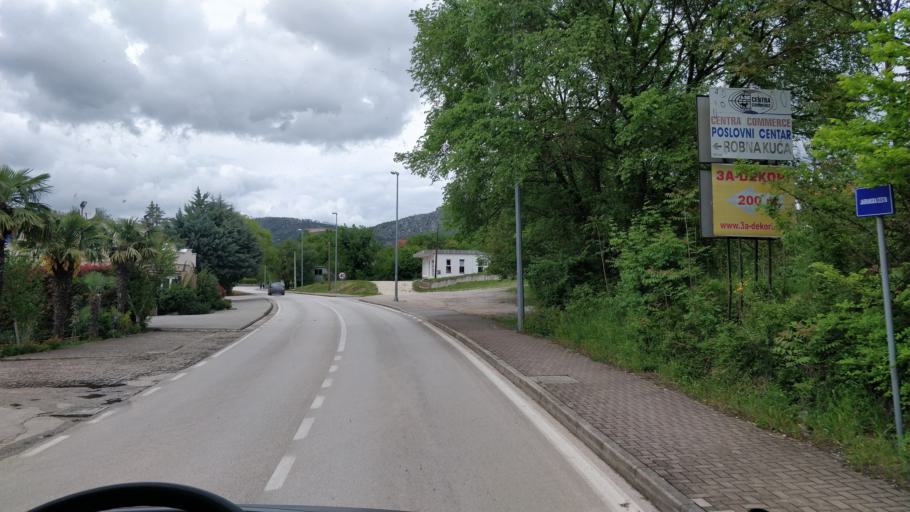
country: BA
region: Federation of Bosnia and Herzegovina
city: Ljubuski
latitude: 43.1870
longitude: 17.5297
